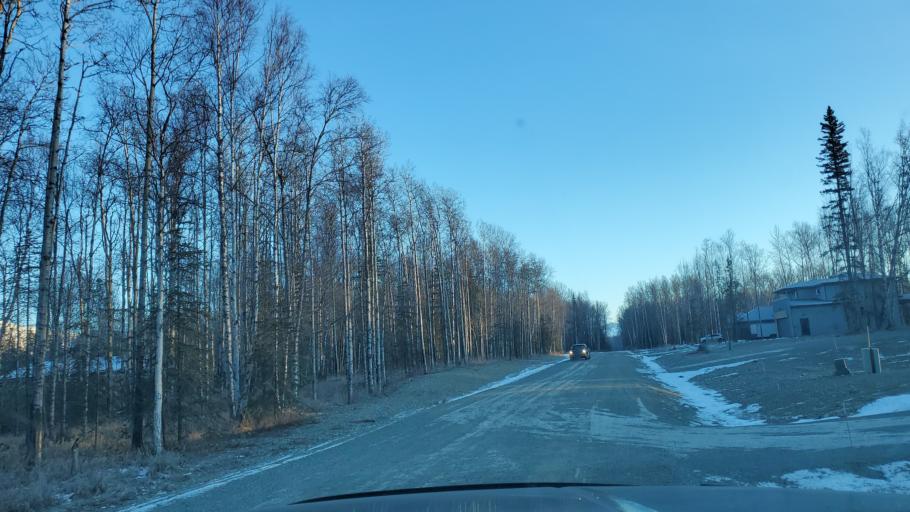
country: US
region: Alaska
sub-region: Matanuska-Susitna Borough
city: Lakes
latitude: 61.6572
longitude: -149.3440
